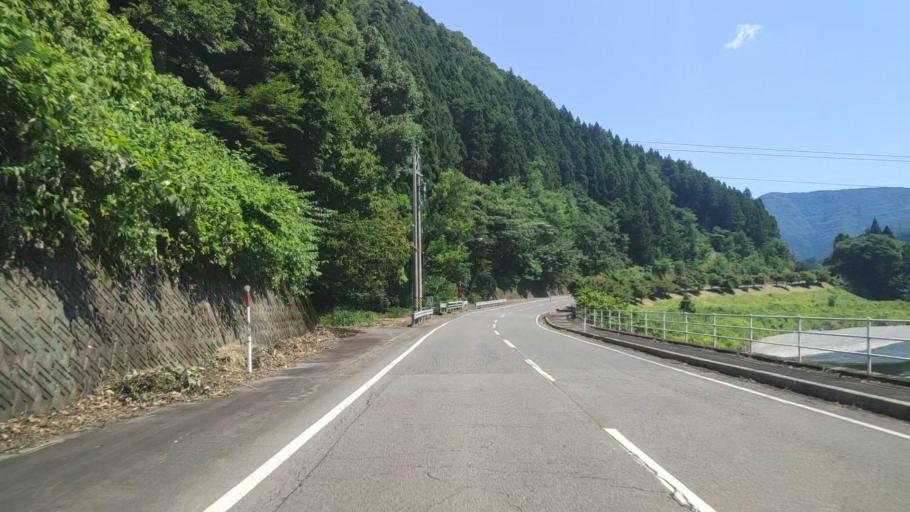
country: JP
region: Gifu
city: Godo
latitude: 35.6015
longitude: 136.6292
